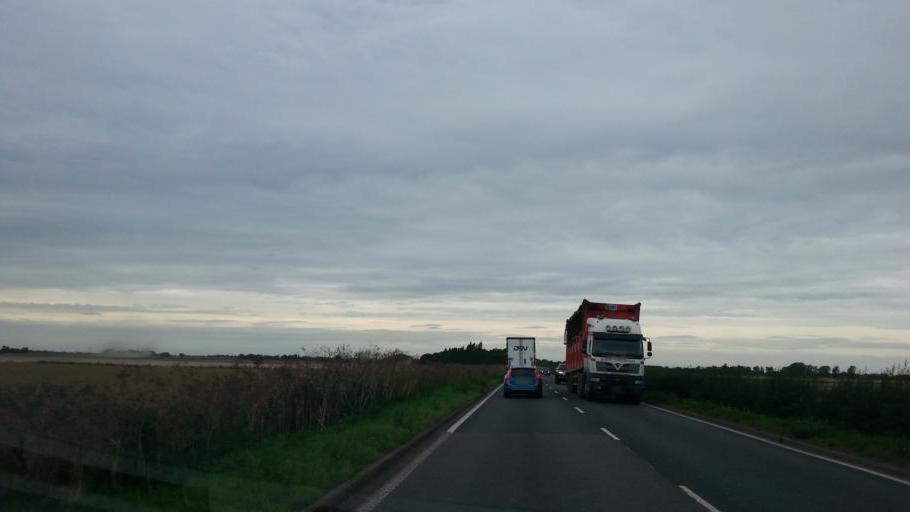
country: GB
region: England
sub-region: Peterborough
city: Thorney
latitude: 52.6189
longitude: -0.0385
